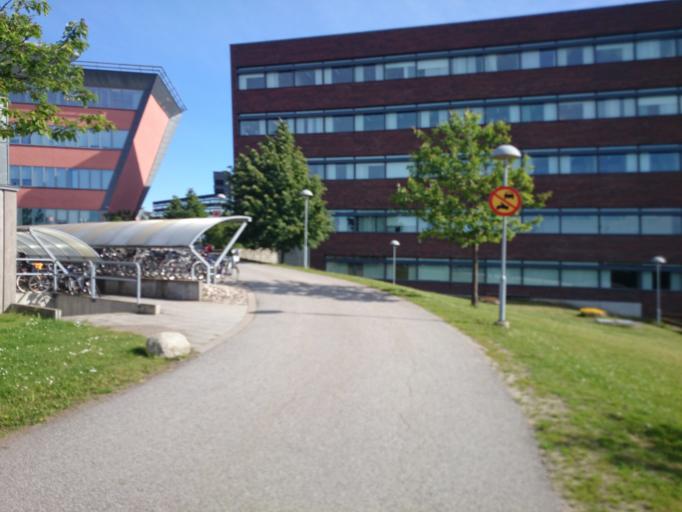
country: SE
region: Skane
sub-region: Lunds Kommun
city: Lund
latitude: 55.7160
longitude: 13.2263
